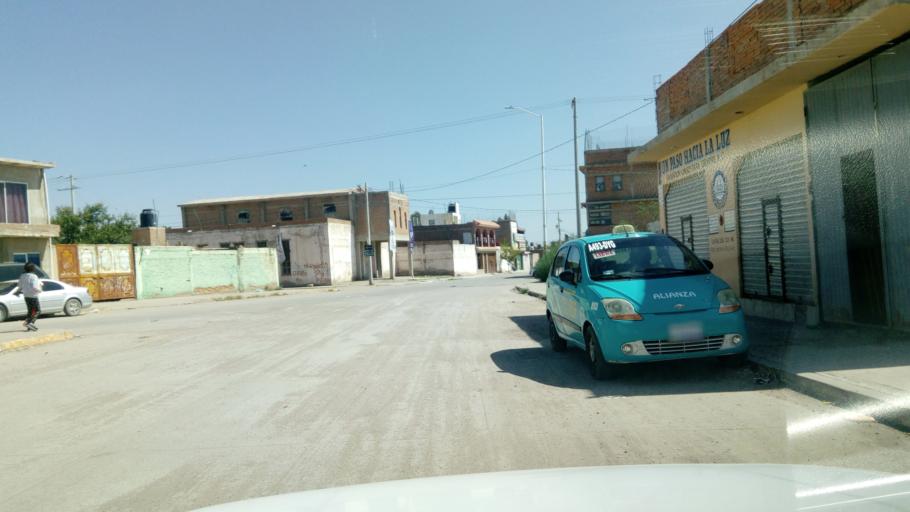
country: MX
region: Durango
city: Victoria de Durango
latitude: 23.9884
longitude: -104.6789
